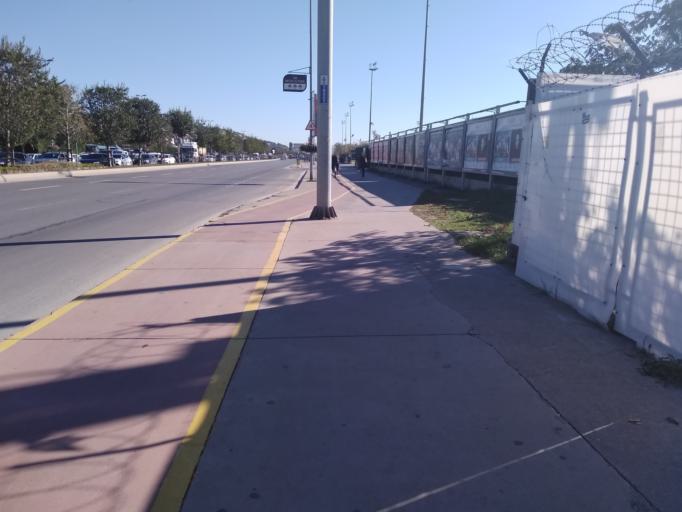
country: TR
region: Istanbul
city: Maltepe
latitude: 40.9194
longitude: 29.1287
